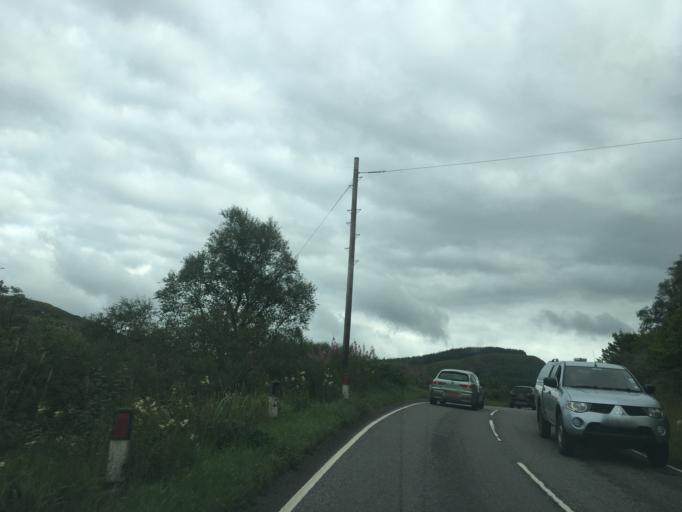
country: GB
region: Scotland
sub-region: Argyll and Bute
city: Oban
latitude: 56.3033
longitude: -5.4668
